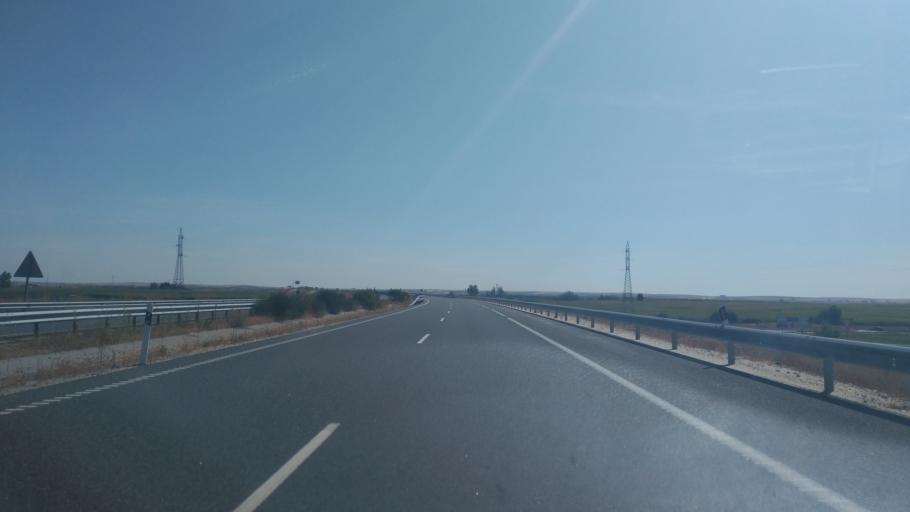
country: ES
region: Castille and Leon
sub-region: Provincia de Salamanca
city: Encinas de Abajo
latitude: 40.9285
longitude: -5.4688
